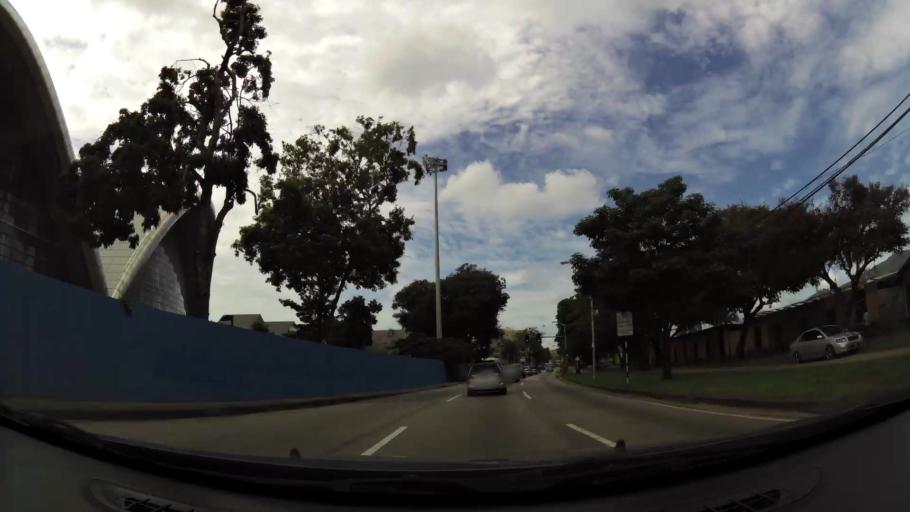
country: TT
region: City of Port of Spain
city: Port-of-Spain
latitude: 10.6641
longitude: -61.5116
